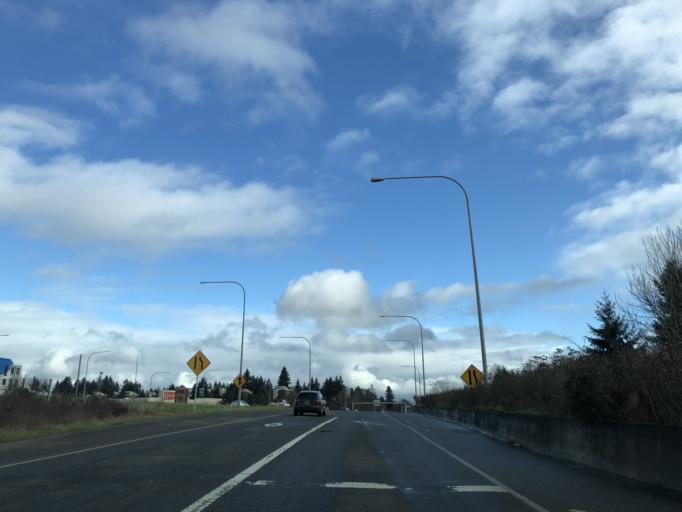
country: US
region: Washington
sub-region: Pierce County
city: Fircrest
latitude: 47.2345
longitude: -122.4807
